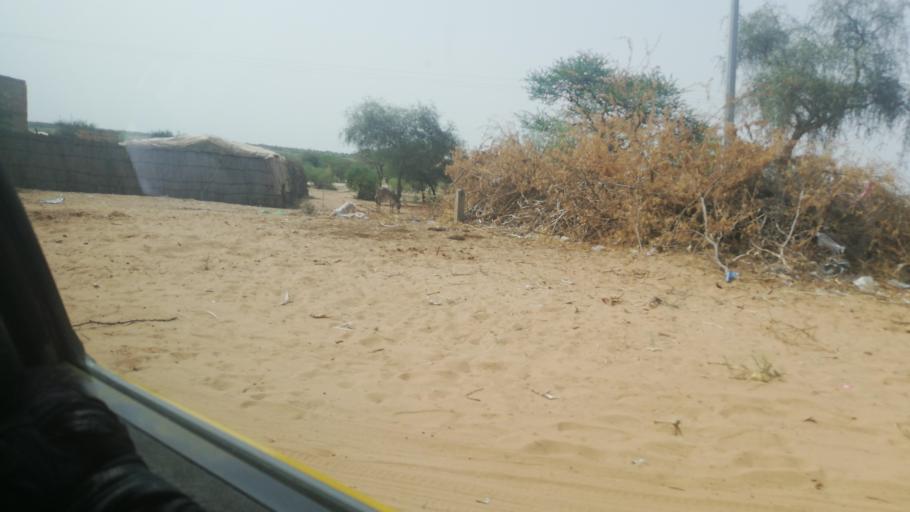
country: SN
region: Saint-Louis
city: Saint-Louis
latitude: 16.0537
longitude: -16.3327
